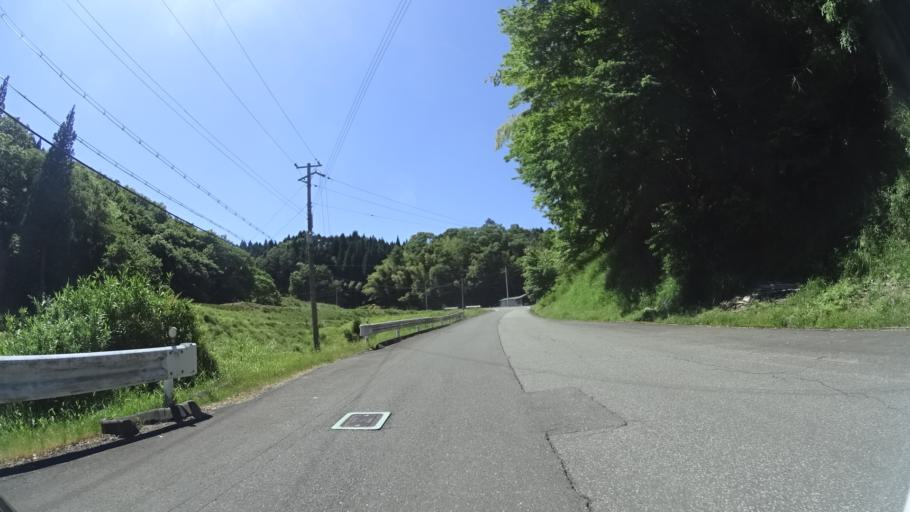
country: JP
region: Kyoto
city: Fukuchiyama
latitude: 35.4298
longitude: 135.0504
